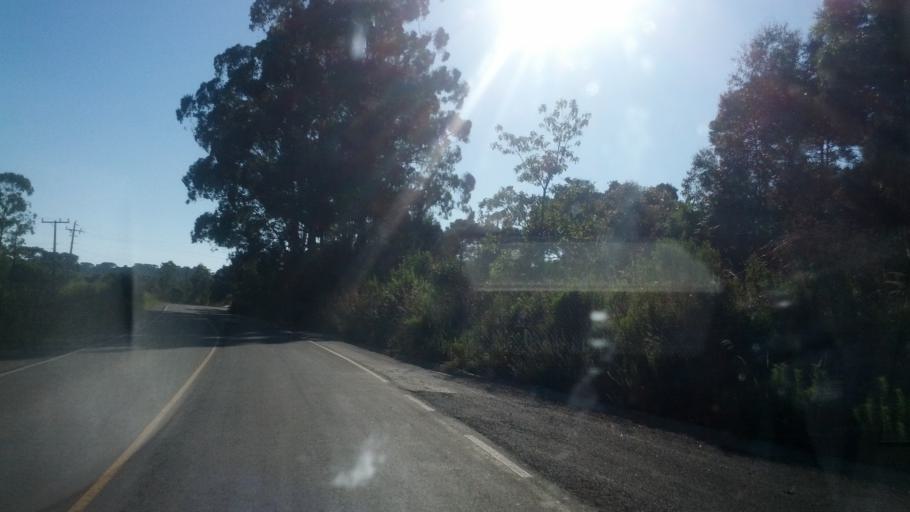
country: BR
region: Santa Catarina
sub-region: Lages
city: Lages
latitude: -27.9267
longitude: -50.5402
